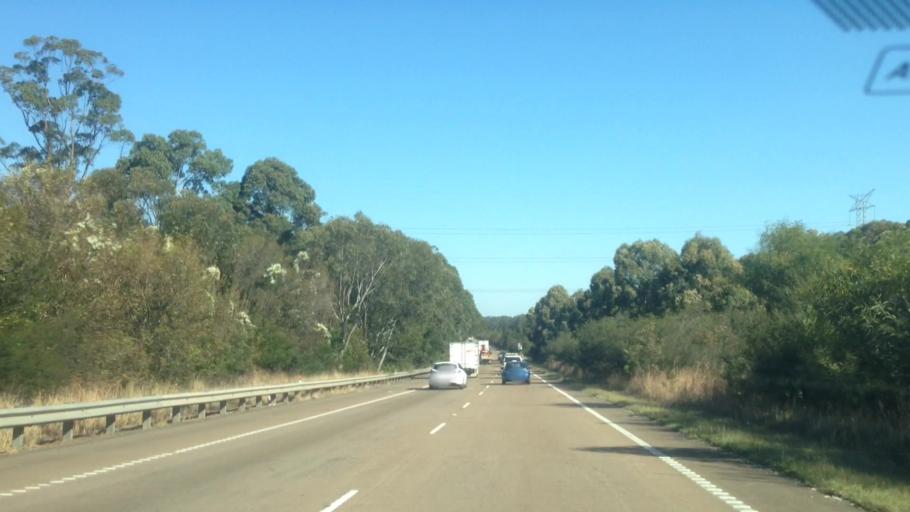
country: AU
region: New South Wales
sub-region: Lake Macquarie Shire
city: Dora Creek
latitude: -33.1551
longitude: 151.4713
